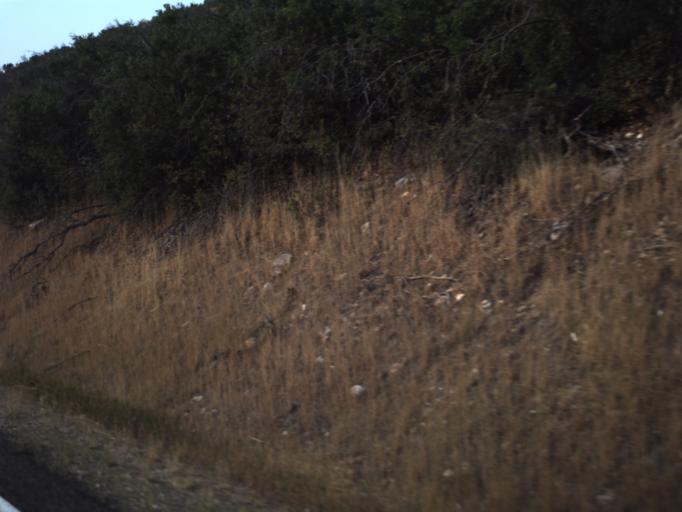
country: US
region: Utah
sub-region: Summit County
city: Kamas
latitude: 40.6333
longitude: -111.2541
